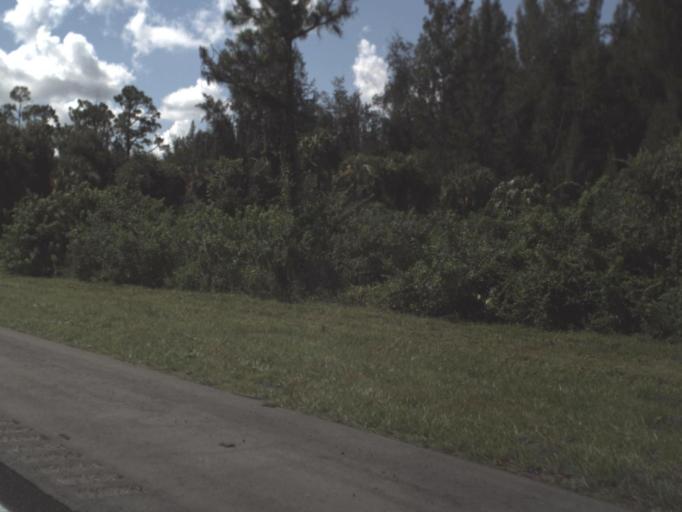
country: US
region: Florida
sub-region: Lee County
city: Suncoast Estates
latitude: 26.7389
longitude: -81.8499
